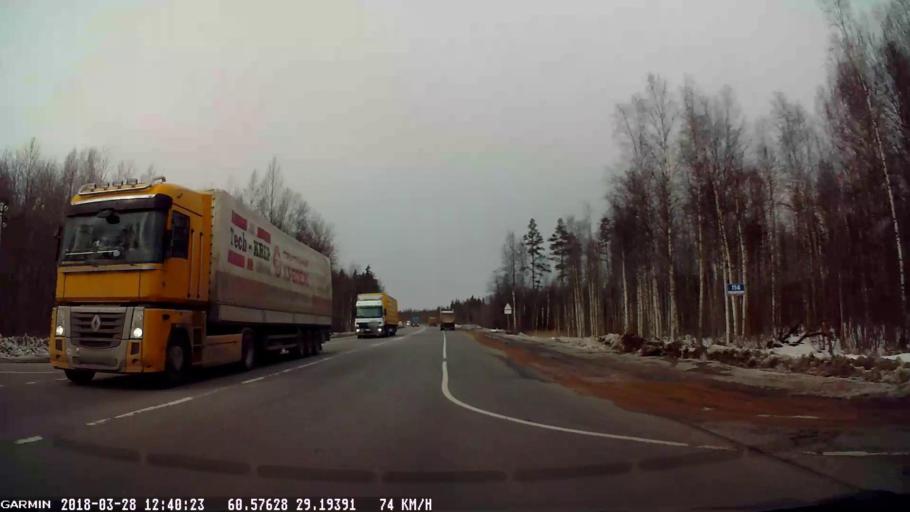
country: RU
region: Leningrad
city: Veshchevo
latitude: 60.5763
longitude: 29.1939
